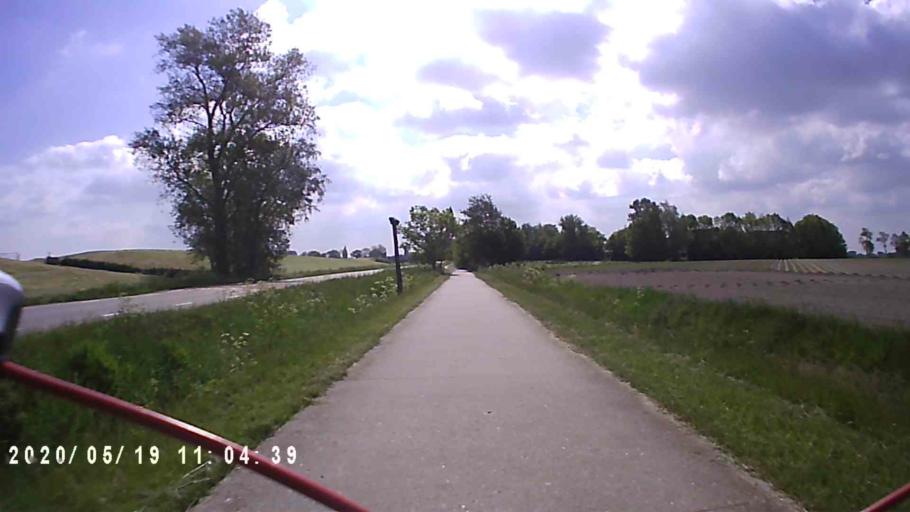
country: NL
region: Groningen
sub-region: Gemeente Zuidhorn
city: Grijpskerk
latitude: 53.2967
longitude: 6.2860
